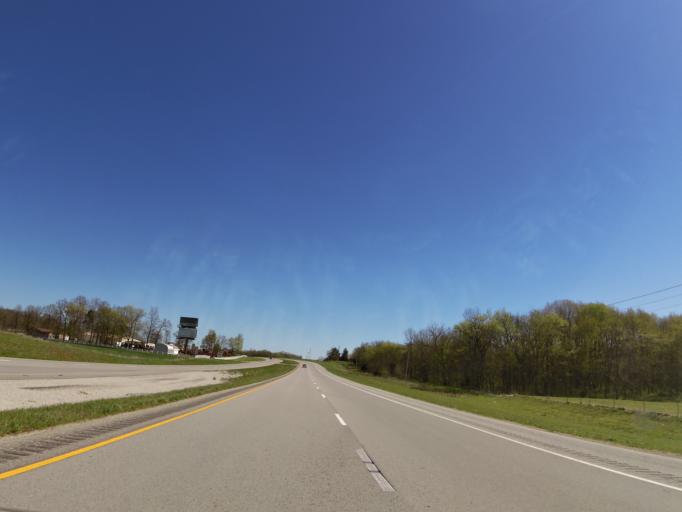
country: US
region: Kentucky
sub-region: Logan County
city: Auburn
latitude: 36.8768
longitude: -86.6736
